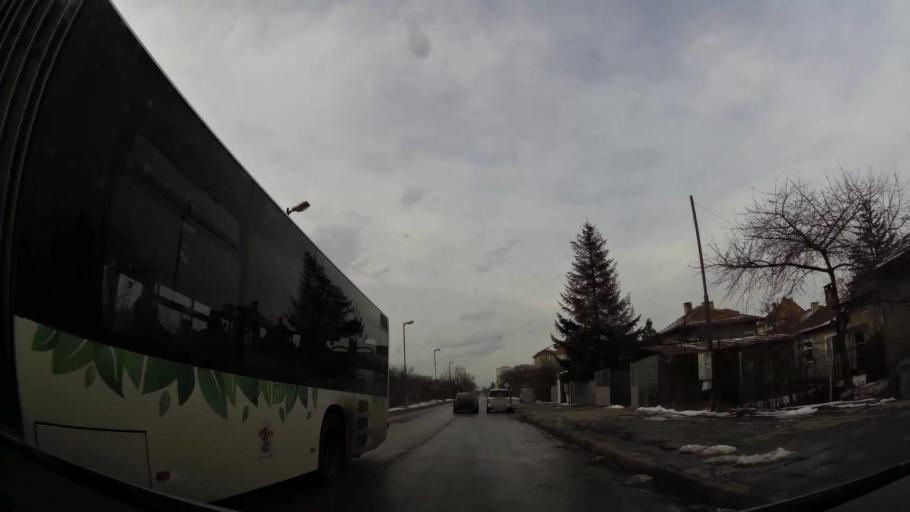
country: BG
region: Sofia-Capital
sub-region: Stolichna Obshtina
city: Sofia
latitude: 42.7021
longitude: 23.3778
